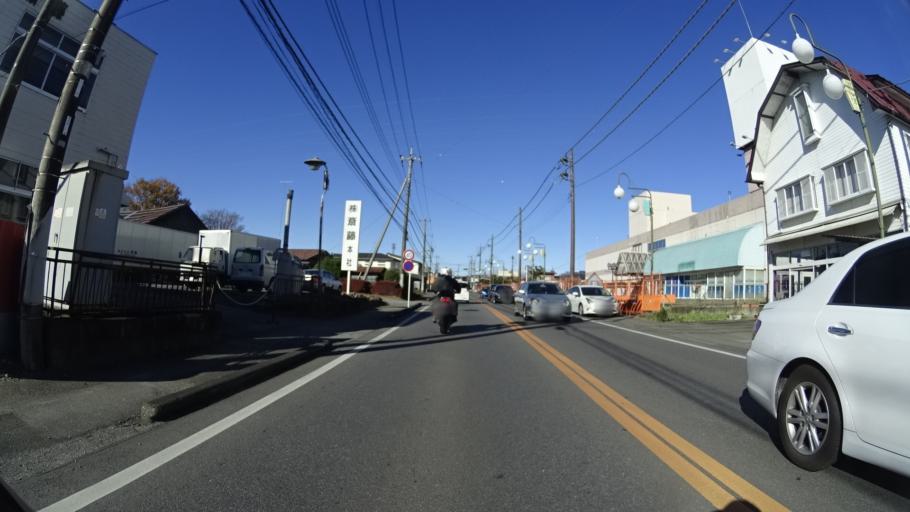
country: JP
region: Tochigi
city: Kanuma
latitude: 36.5519
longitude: 139.7470
